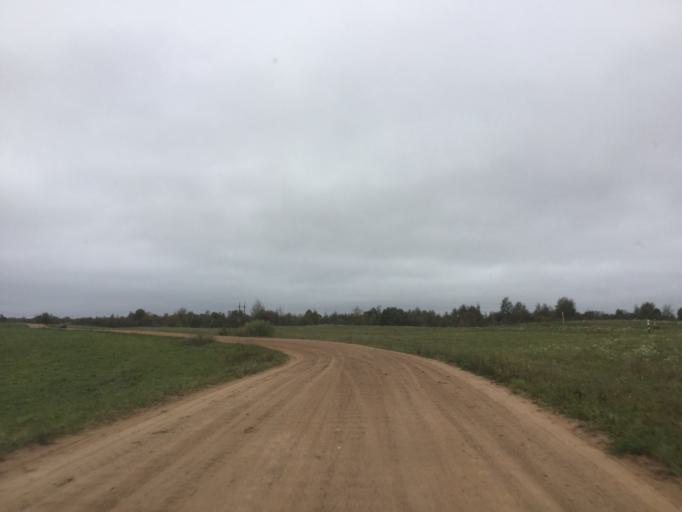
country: BY
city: Novolukoml'
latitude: 54.7137
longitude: 29.1258
